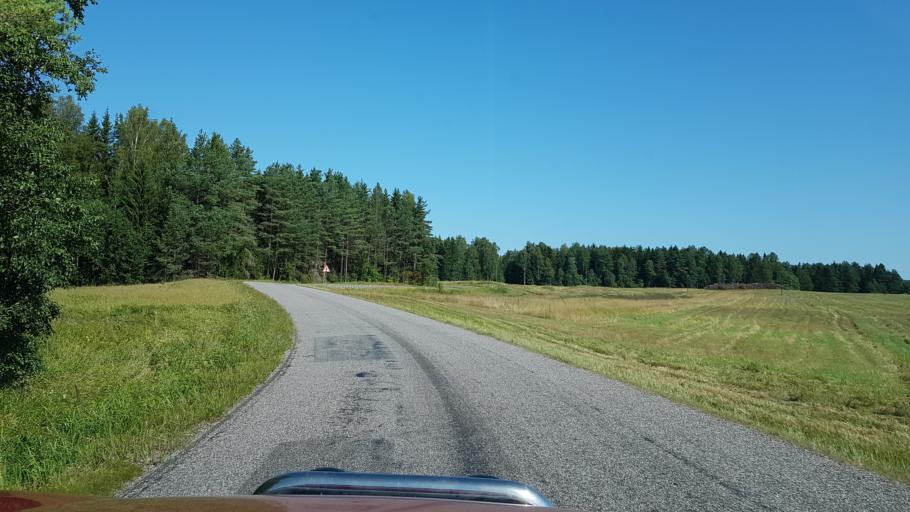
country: EE
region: Vorumaa
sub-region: Voru linn
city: Voru
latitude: 57.7240
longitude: 27.2106
